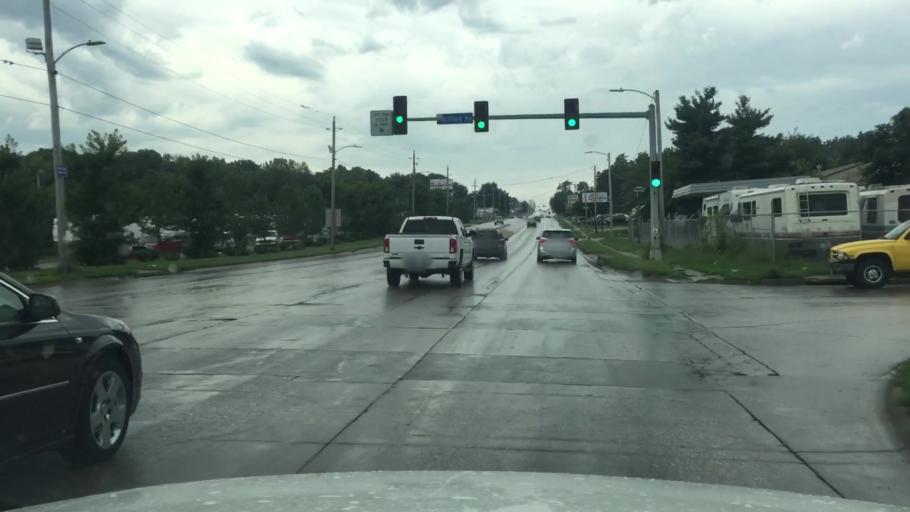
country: US
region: Iowa
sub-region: Polk County
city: Des Moines
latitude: 41.5698
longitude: -93.5971
